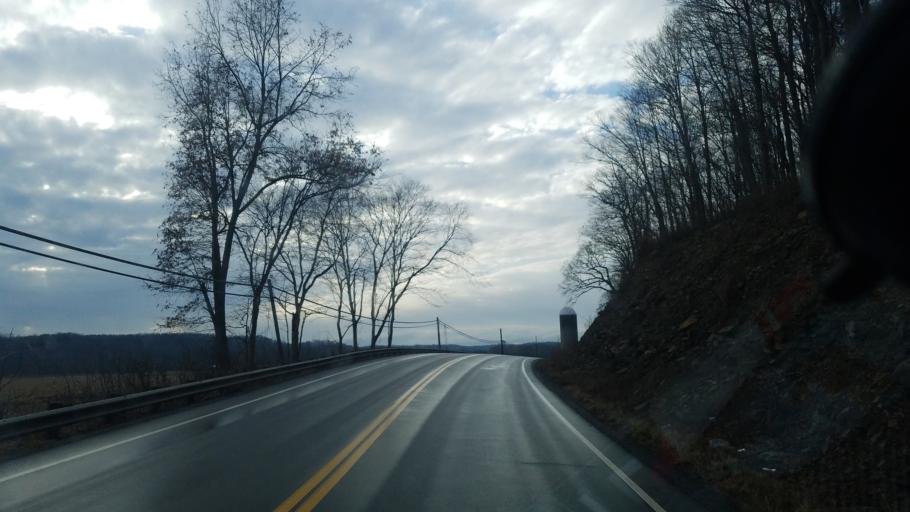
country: US
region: Ohio
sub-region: Coshocton County
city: Coshocton
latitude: 40.3407
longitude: -82.0209
